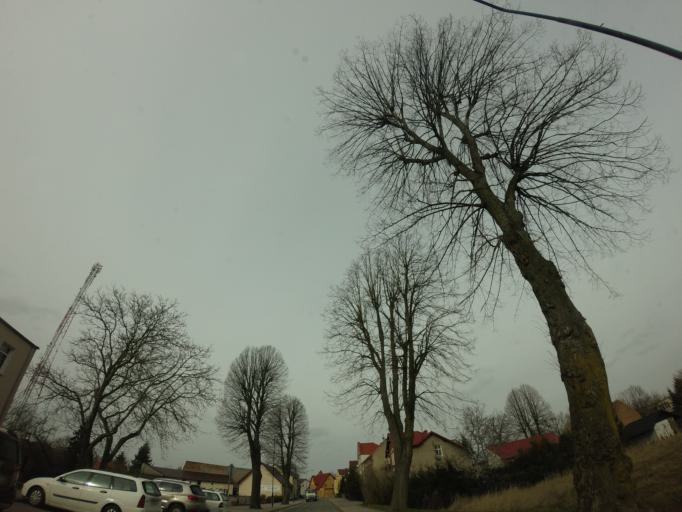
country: PL
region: West Pomeranian Voivodeship
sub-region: Powiat drawski
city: Drawsko Pomorskie
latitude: 53.5238
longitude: 15.8160
